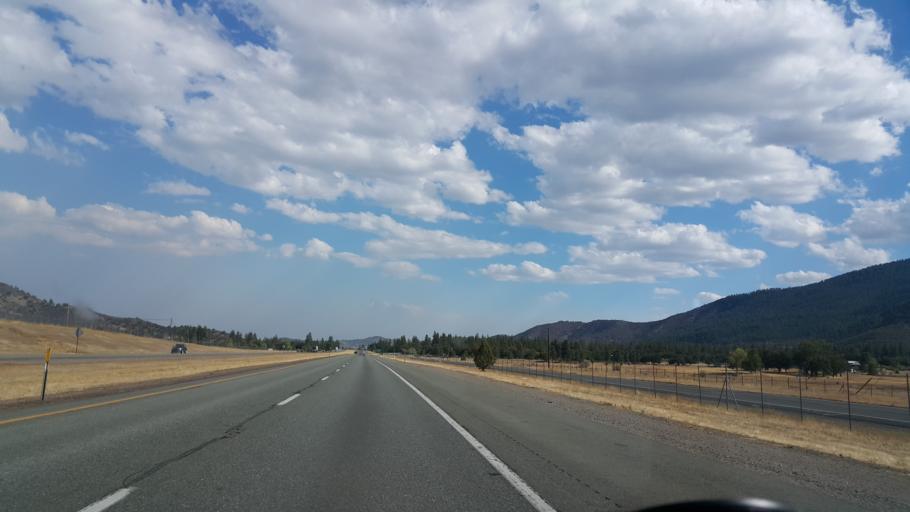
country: US
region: California
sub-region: Siskiyou County
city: Yreka
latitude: 41.6744
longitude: -122.6217
